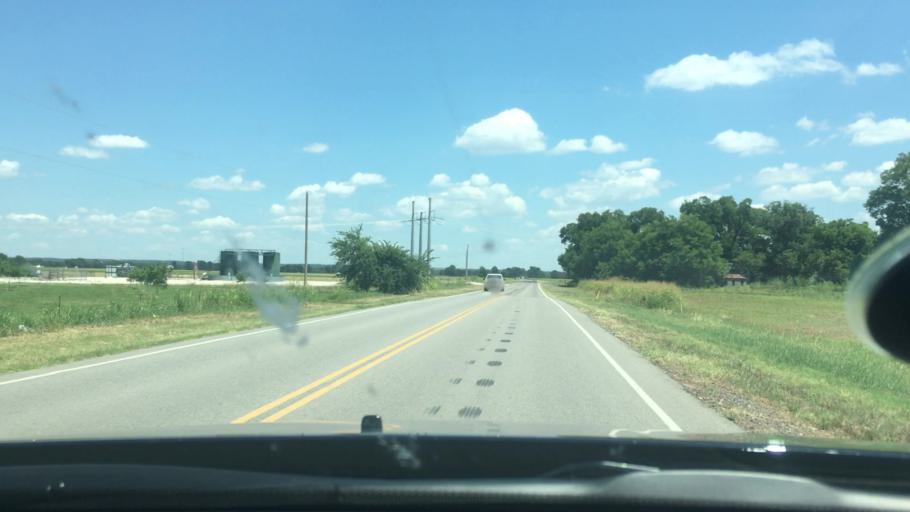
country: US
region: Oklahoma
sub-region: Carter County
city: Dickson
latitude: 34.2432
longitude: -96.9739
